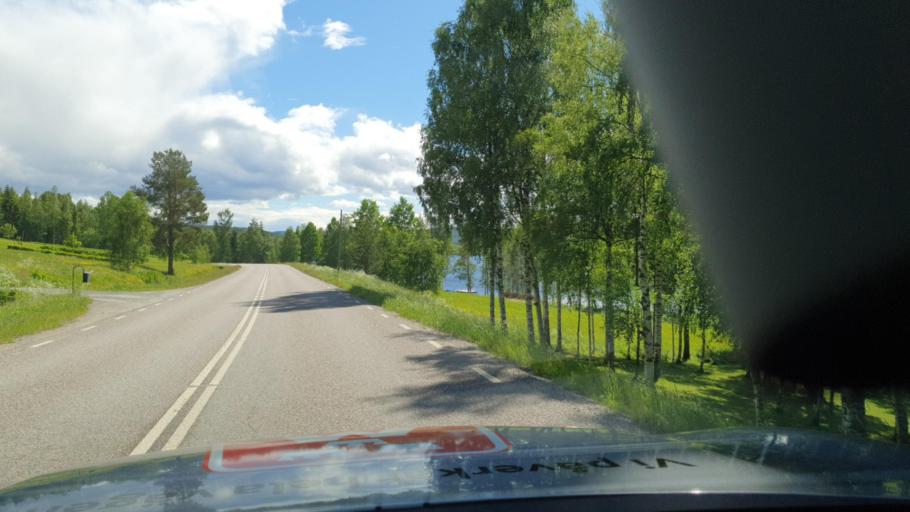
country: SE
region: Vaesternorrland
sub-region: OErnskoeldsviks Kommun
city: Bjasta
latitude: 63.2750
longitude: 18.2881
